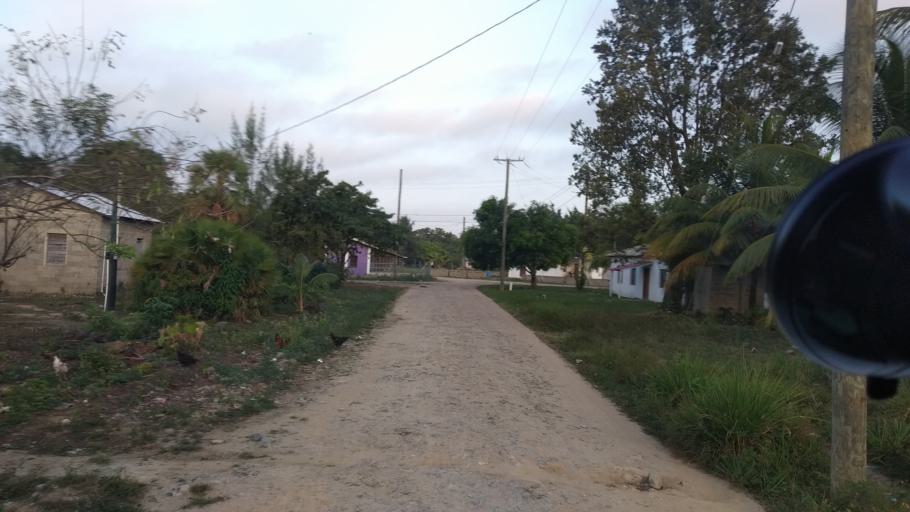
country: BZ
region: Stann Creek
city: Placencia
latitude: 16.5706
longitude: -88.5255
